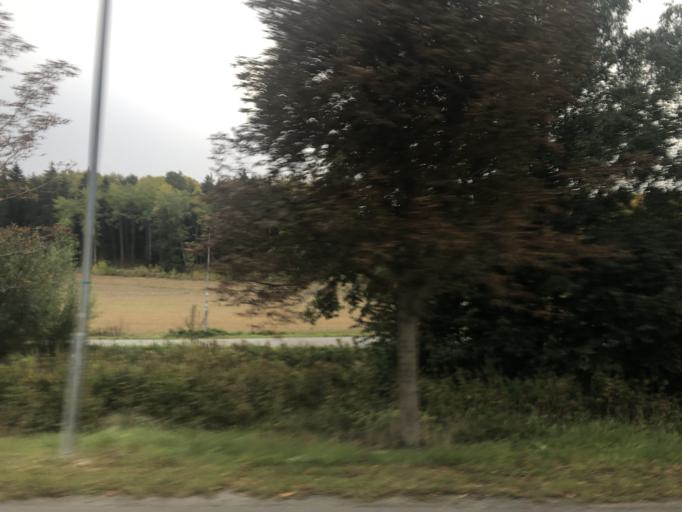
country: SE
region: Stockholm
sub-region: Jarfalla Kommun
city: Jakobsberg
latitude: 59.4179
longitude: 17.8195
